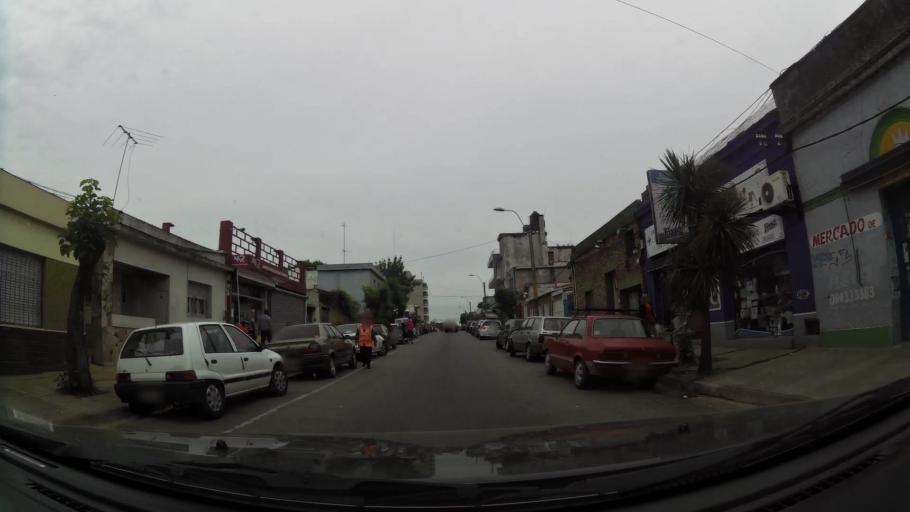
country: UY
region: Canelones
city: Las Piedras
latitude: -34.7263
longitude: -56.2138
